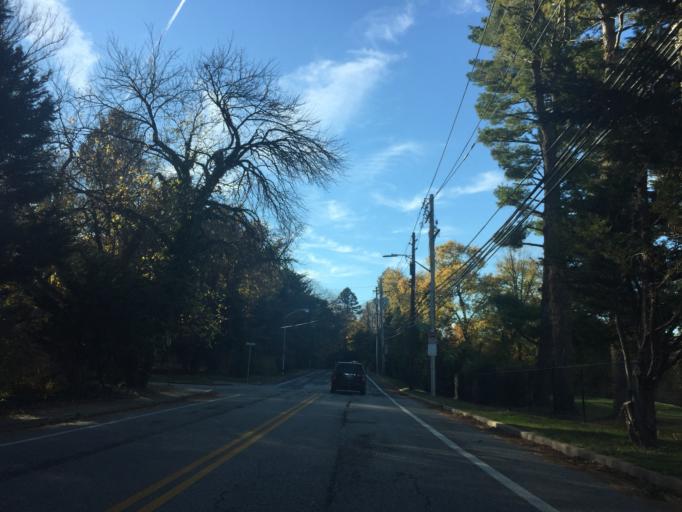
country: US
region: Maryland
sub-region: Baltimore County
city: Towson
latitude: 39.3687
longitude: -76.6310
